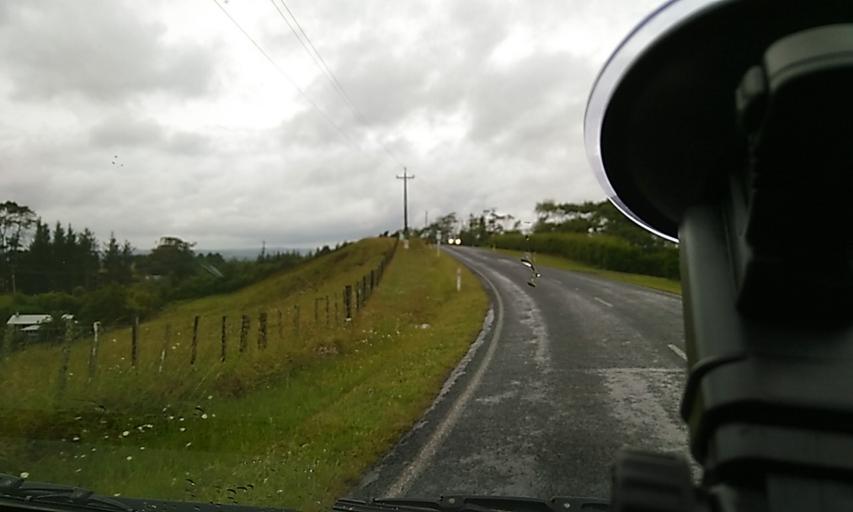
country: NZ
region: Auckland
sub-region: Auckland
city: Pukekohe East
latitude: -37.3224
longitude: 174.9198
